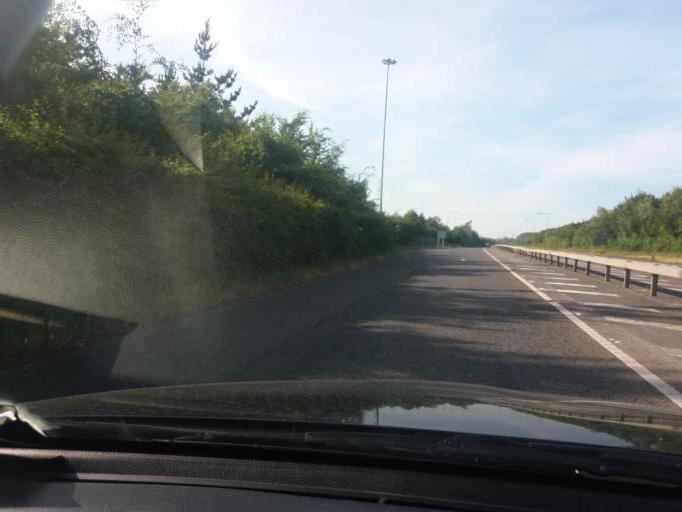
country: IE
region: Leinster
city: Balrothery
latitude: 53.5509
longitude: -6.2093
